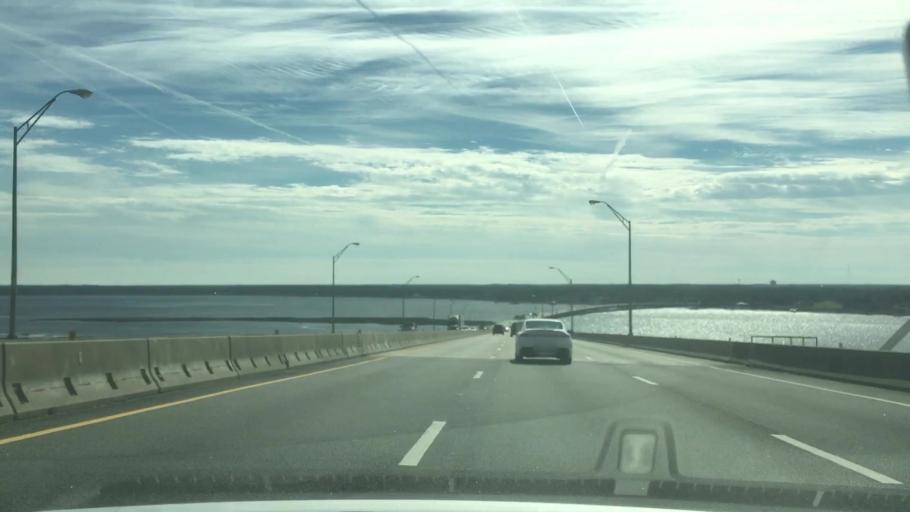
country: US
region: Florida
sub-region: Duval County
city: Jacksonville
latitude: 30.3813
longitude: -81.5558
